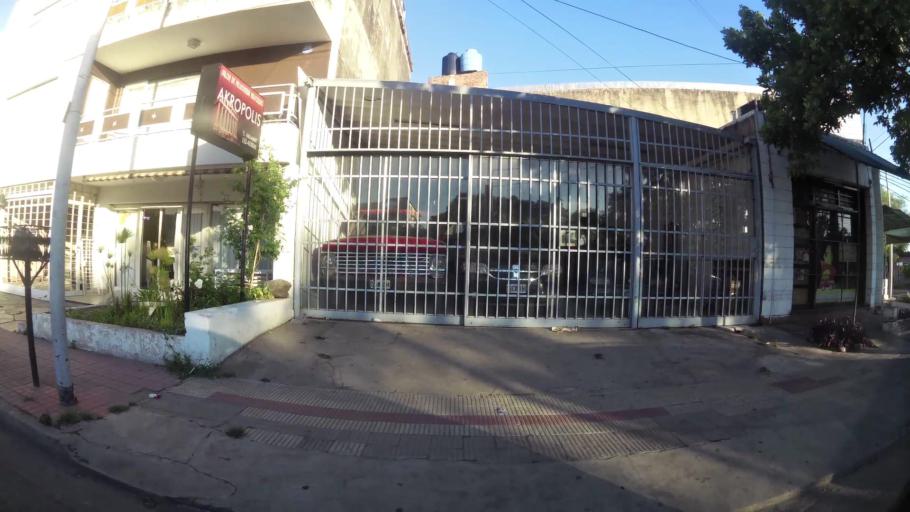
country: AR
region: Cordoba
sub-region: Departamento de Capital
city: Cordoba
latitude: -31.3867
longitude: -64.2179
